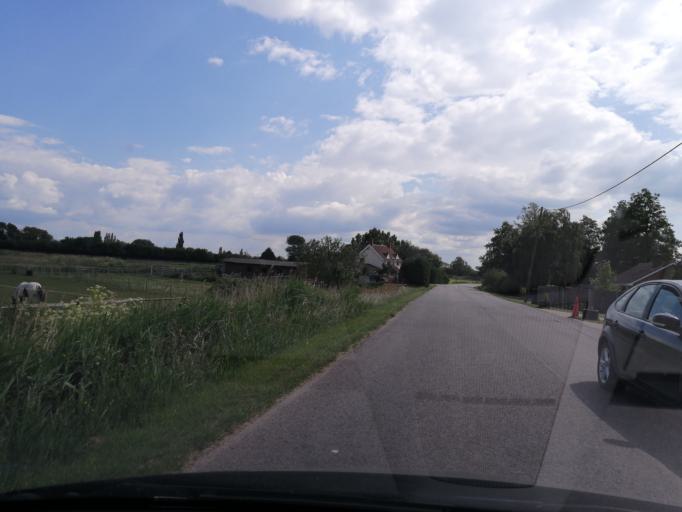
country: GB
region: England
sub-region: Cambridgeshire
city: Ramsey
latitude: 52.4491
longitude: -0.1588
